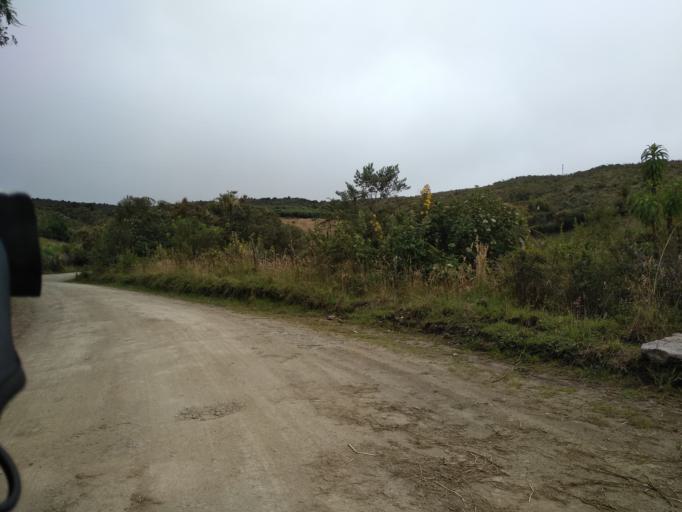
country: EC
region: Carchi
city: Tulcan
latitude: 0.7411
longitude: -77.7849
